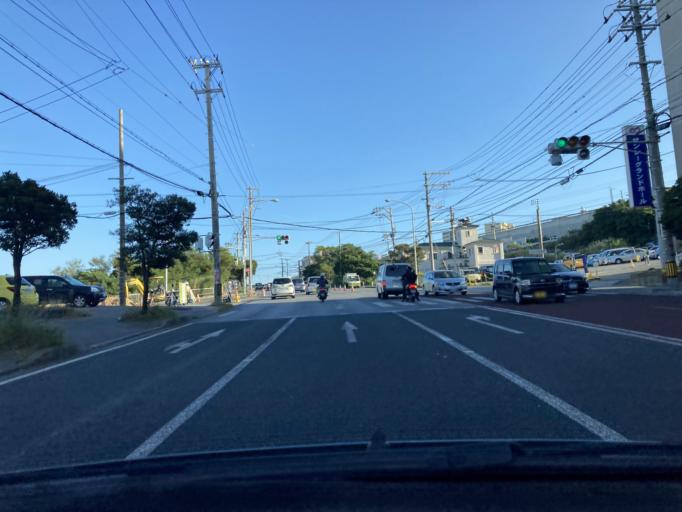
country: JP
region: Okinawa
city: Ginowan
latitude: 26.2442
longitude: 127.7382
